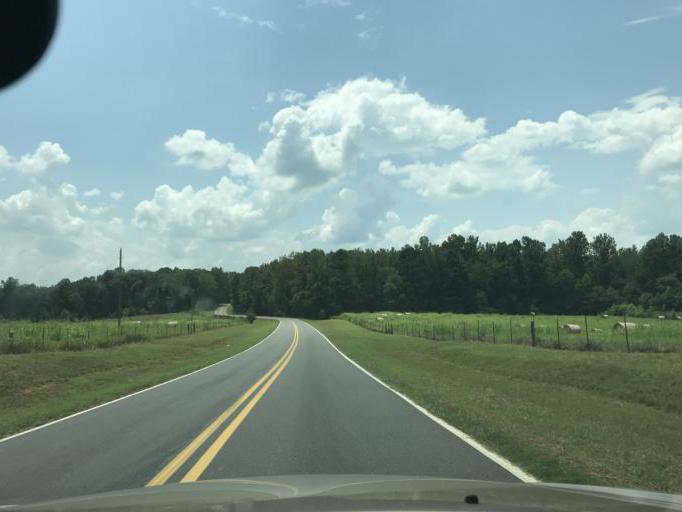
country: US
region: Georgia
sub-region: Forsyth County
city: Cumming
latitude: 34.3207
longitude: -84.2209
